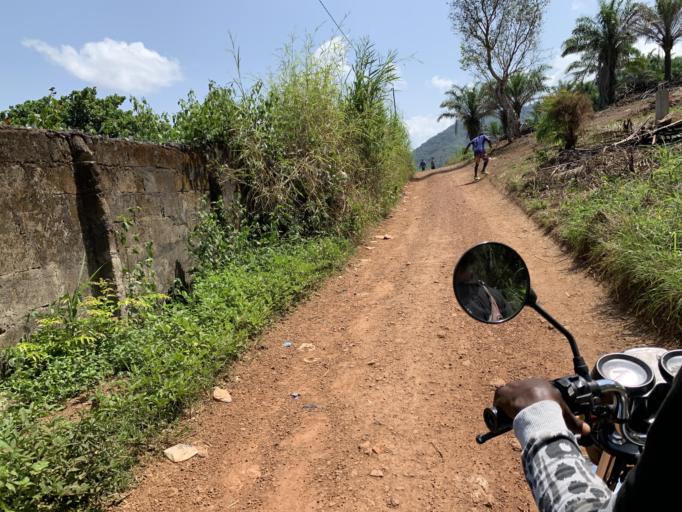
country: SL
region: Western Area
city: Hastings
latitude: 8.3709
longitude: -13.1301
